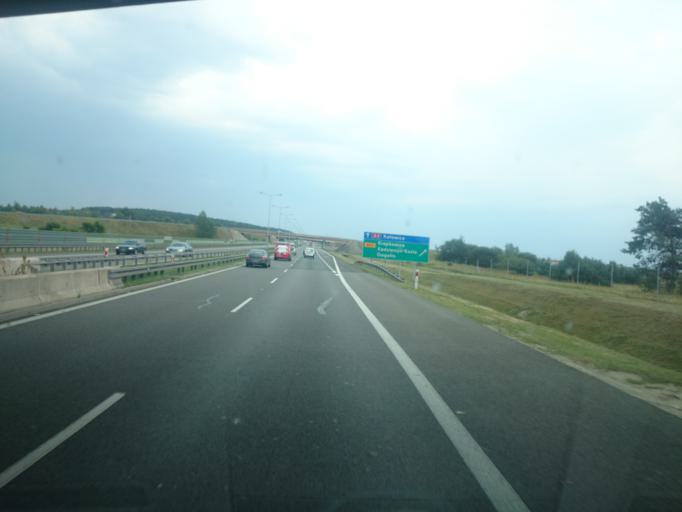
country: PL
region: Opole Voivodeship
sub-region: Powiat krapkowicki
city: Krapkowice
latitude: 50.4894
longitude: 17.9856
